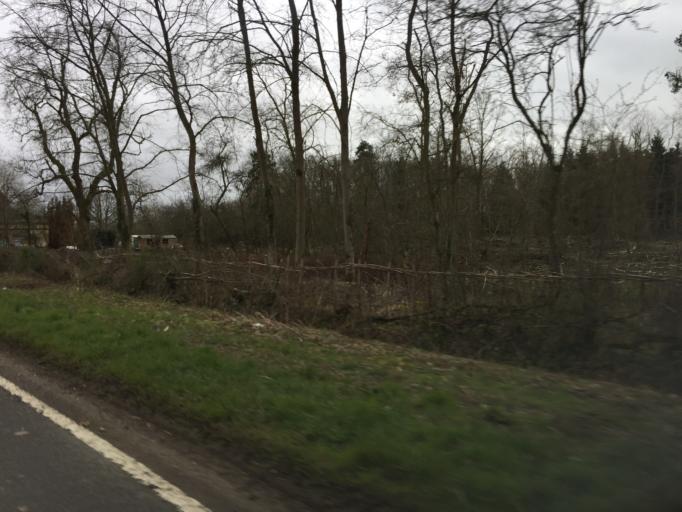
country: GB
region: England
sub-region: Oxfordshire
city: Faringdon
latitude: 51.6696
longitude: -1.6153
